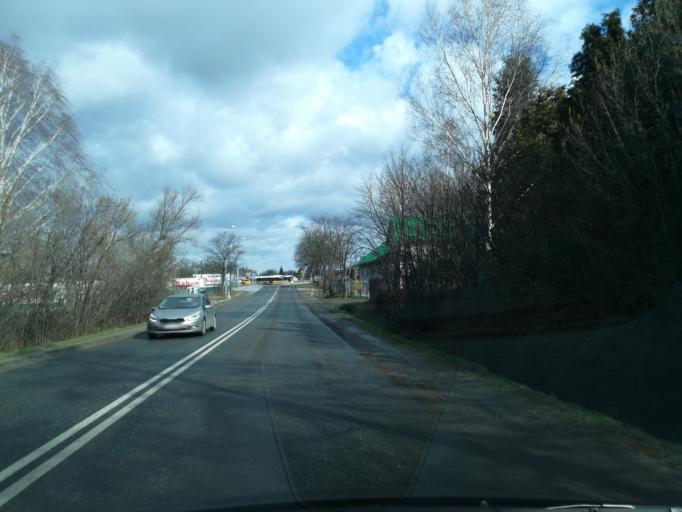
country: PL
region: Lesser Poland Voivodeship
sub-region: Powiat krakowski
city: Kryspinow
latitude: 50.0606
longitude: 19.8038
